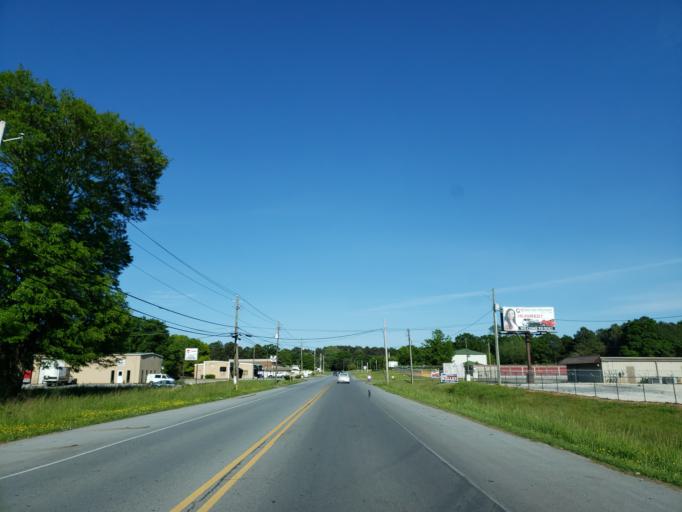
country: US
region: Georgia
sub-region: Polk County
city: Cedartown
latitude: 34.0141
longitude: -85.2347
